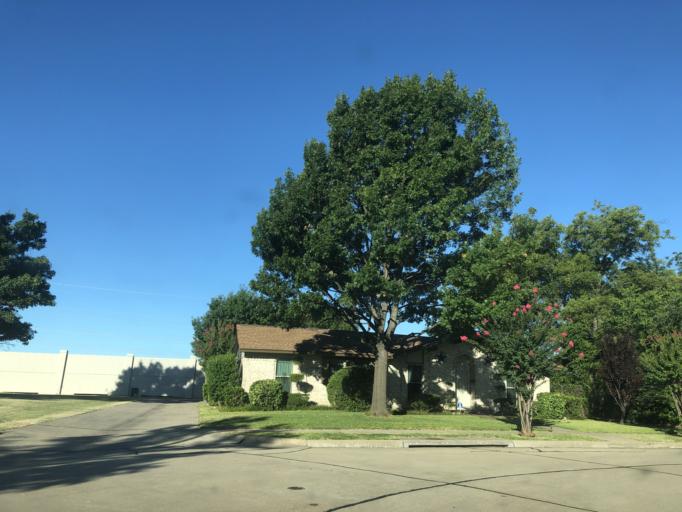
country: US
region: Texas
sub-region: Dallas County
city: Garland
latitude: 32.8476
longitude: -96.6367
